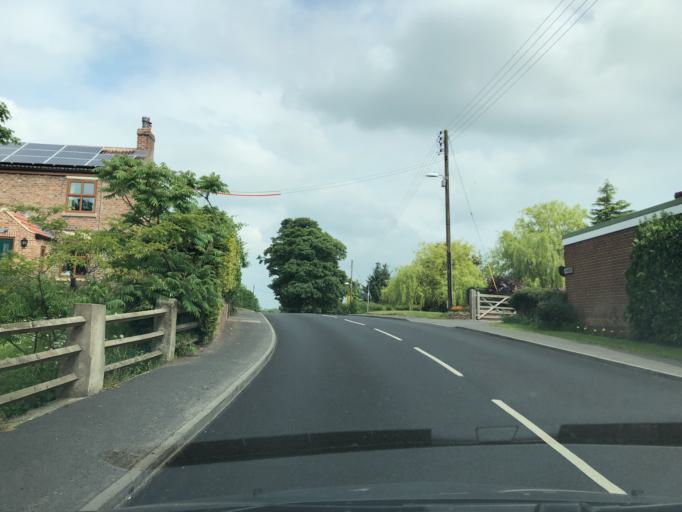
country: GB
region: England
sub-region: North Yorkshire
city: Thirsk
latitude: 54.1802
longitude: -1.3875
